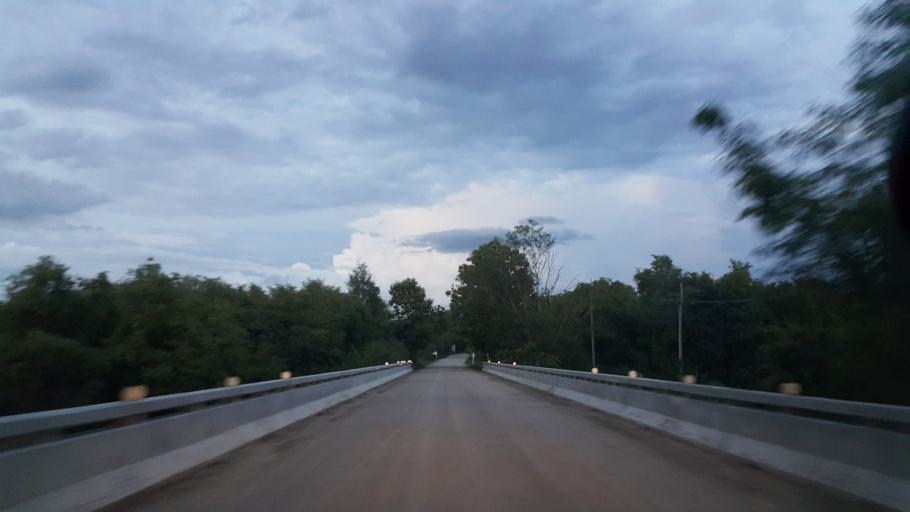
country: TH
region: Loei
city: Phu Ruea
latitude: 17.5321
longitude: 101.2248
